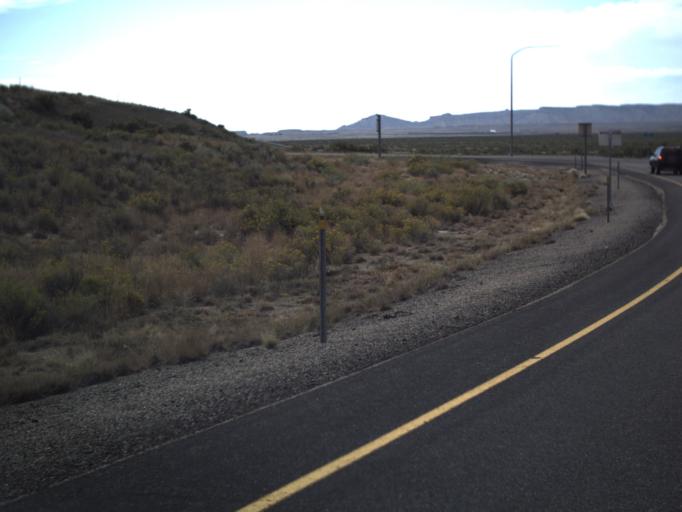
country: US
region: Utah
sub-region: Grand County
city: Moab
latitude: 38.9629
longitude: -109.7209
